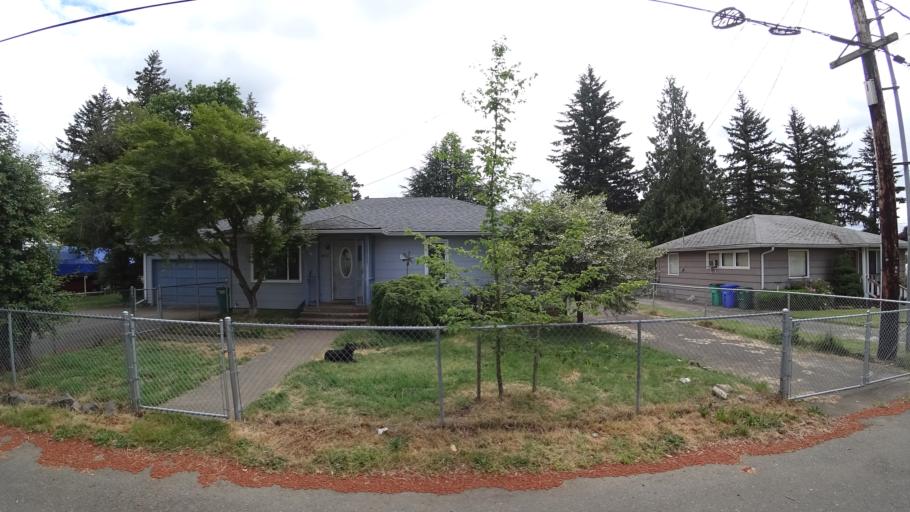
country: US
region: Oregon
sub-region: Multnomah County
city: Lents
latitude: 45.4982
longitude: -122.5332
